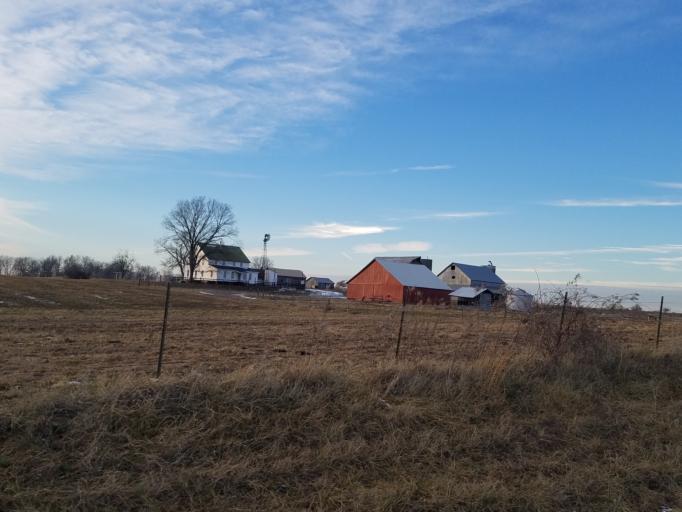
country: US
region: Missouri
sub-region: Randolph County
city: Moberly
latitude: 39.3274
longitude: -92.3033
